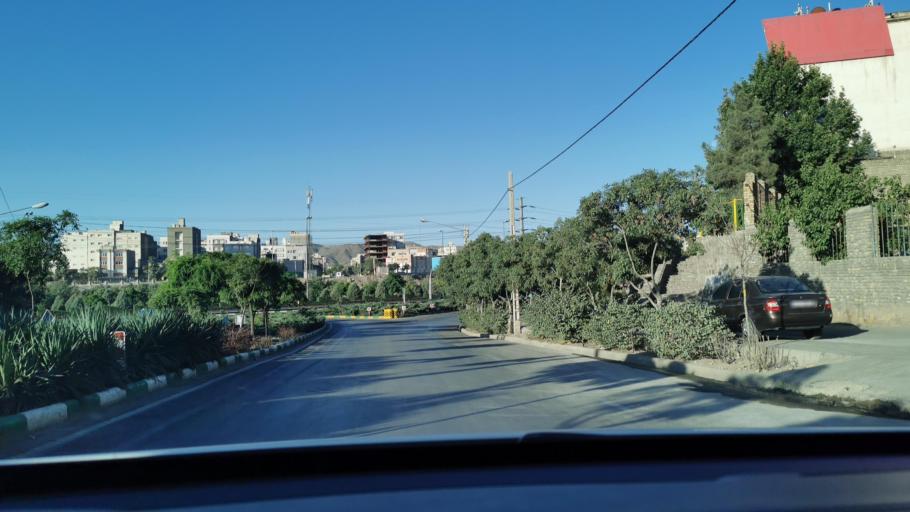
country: IR
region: Razavi Khorasan
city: Mashhad
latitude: 36.3479
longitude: 59.4772
